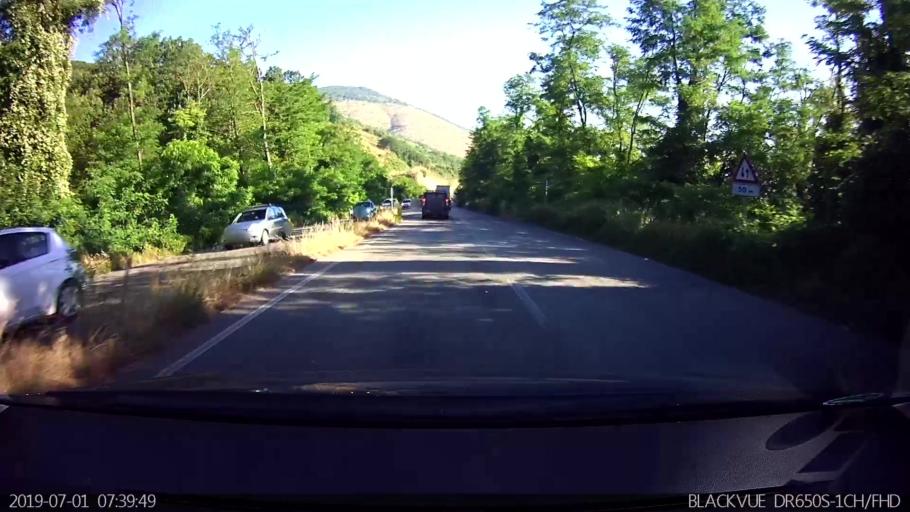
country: IT
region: Latium
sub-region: Provincia di Frosinone
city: Giuliano di Roma
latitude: 41.5524
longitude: 13.2674
